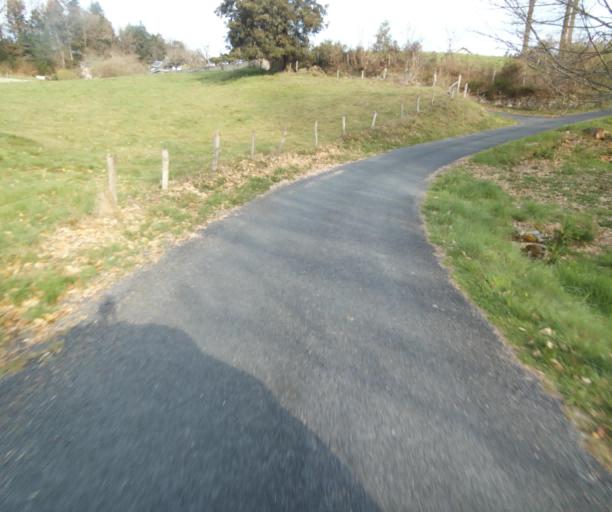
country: FR
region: Limousin
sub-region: Departement de la Correze
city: Correze
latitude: 45.3743
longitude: 1.8712
